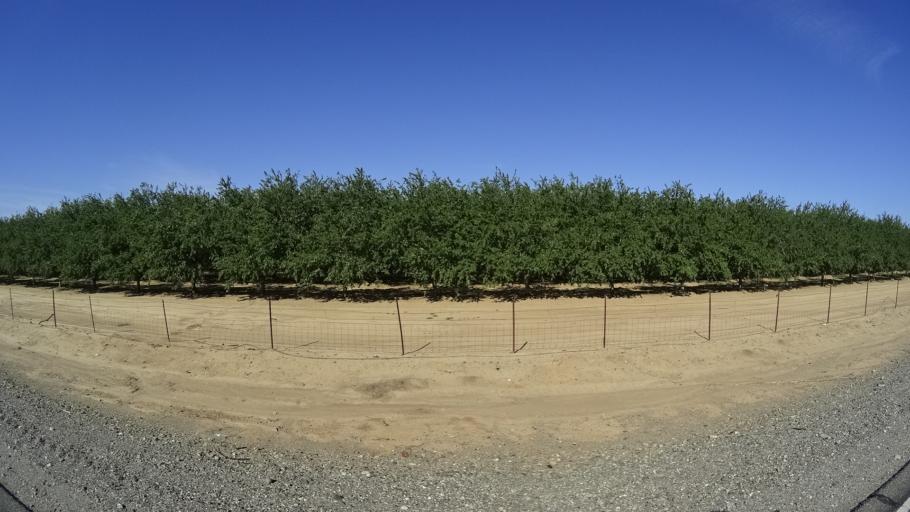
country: US
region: California
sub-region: Glenn County
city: Orland
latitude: 39.6734
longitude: -122.1970
